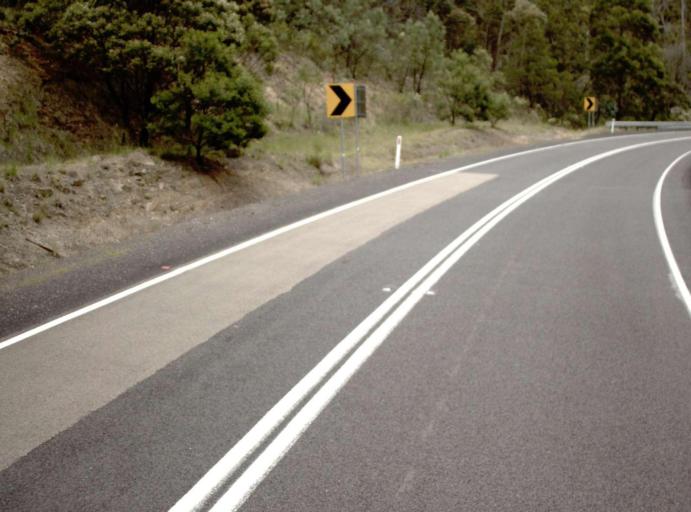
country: AU
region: New South Wales
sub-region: Bombala
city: Bombala
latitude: -37.2495
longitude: 149.2531
